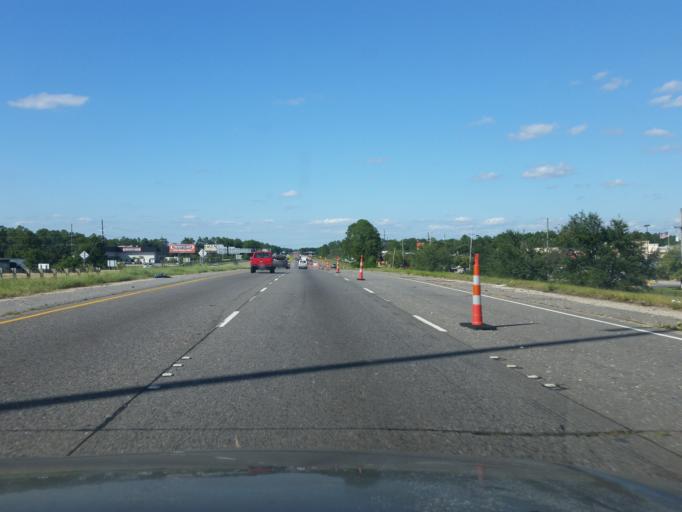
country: US
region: Louisiana
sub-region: Saint Tammany Parish
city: Slidell
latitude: 30.2850
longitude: -89.7493
